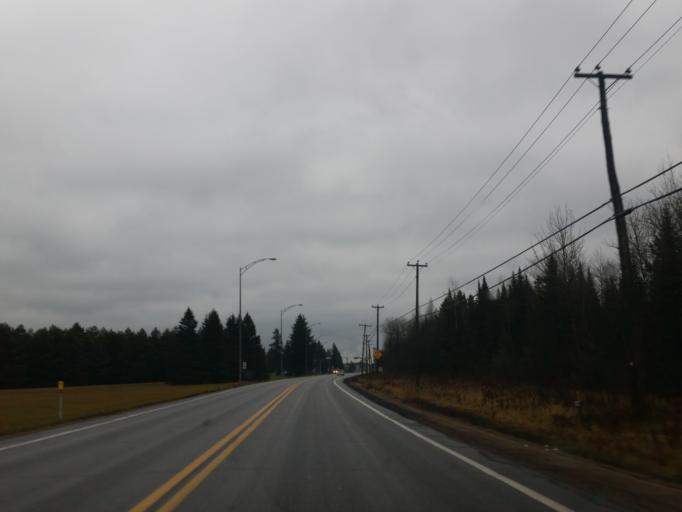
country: CA
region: Quebec
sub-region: Capitale-Nationale
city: Shannon
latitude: 46.8852
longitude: -71.4927
